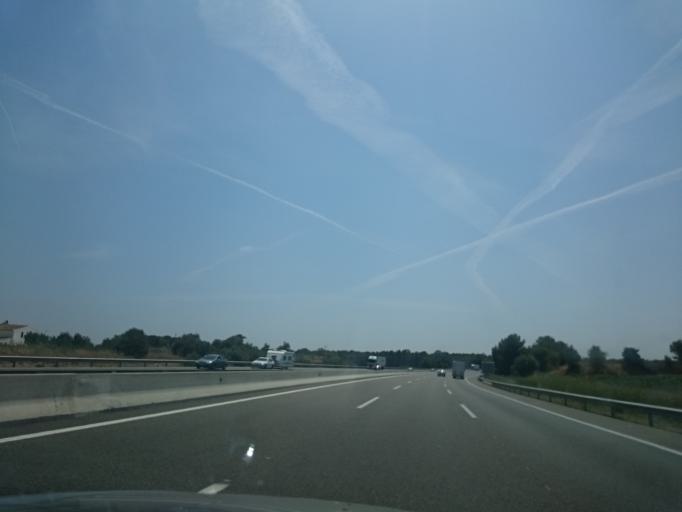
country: ES
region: Catalonia
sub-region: Provincia de Tarragona
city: Sant Jaume dels Domenys
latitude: 41.2951
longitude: 1.5991
